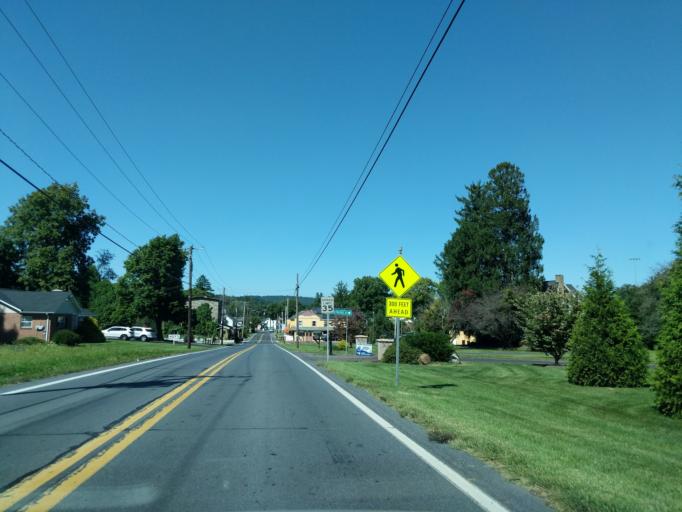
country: US
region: Pennsylvania
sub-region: Lehigh County
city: Coopersburg
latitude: 40.5064
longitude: -75.4460
